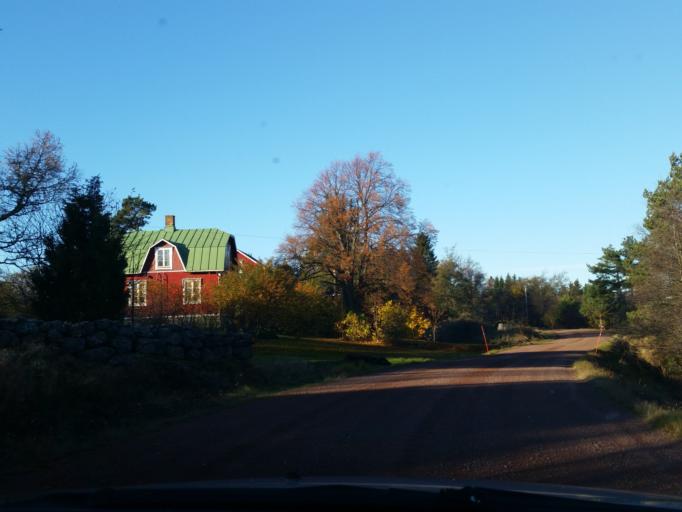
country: AX
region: Alands skaergard
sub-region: Braendoe
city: Braendoe
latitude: 60.4528
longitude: 20.9489
